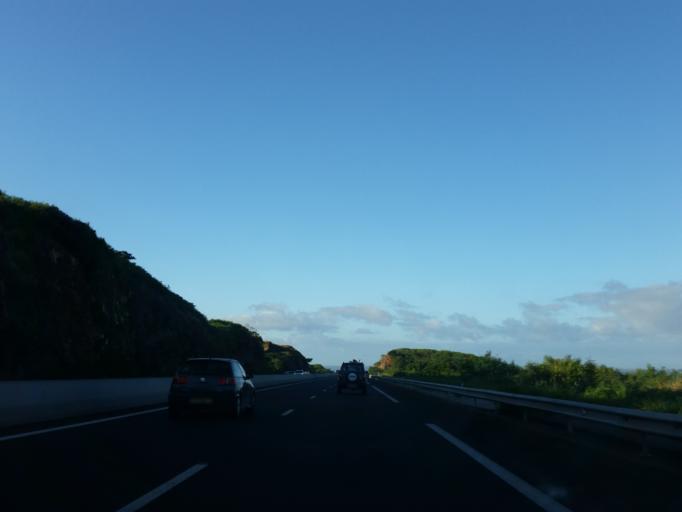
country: RE
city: Piton Saint-Leu
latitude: -21.2337
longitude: 55.3125
